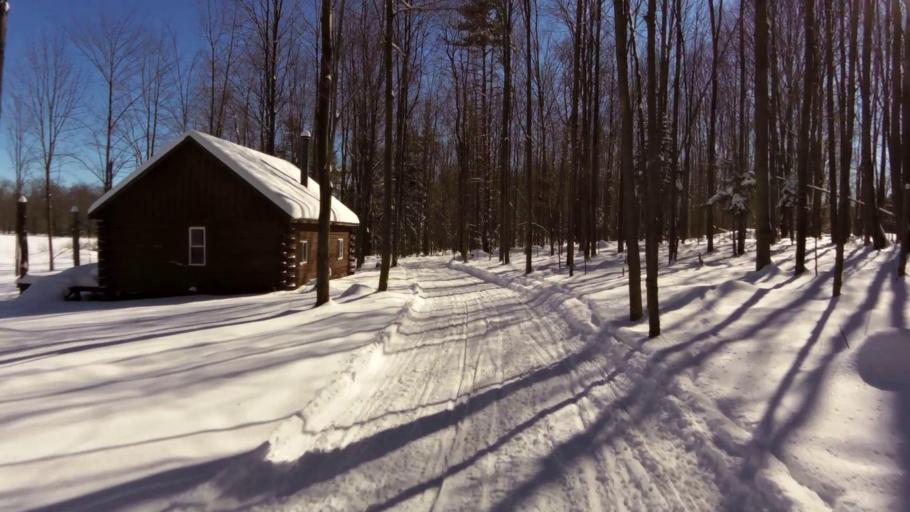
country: US
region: New York
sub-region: Chautauqua County
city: Mayville
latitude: 42.2342
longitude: -79.5213
